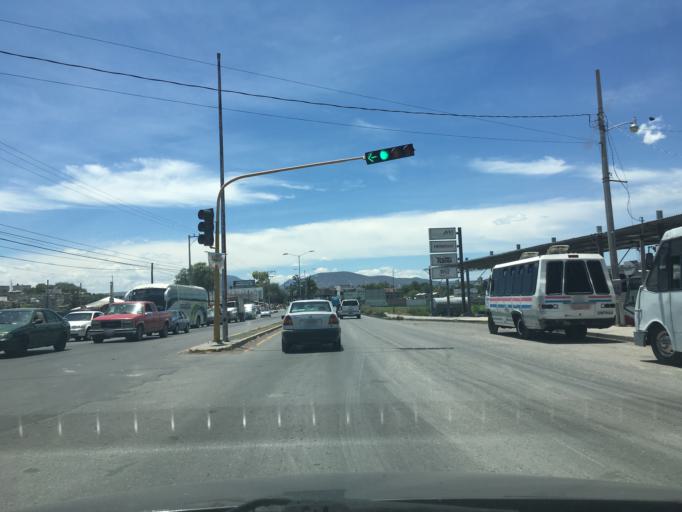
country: MX
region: Hidalgo
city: Ixmiquilpan
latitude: 20.4797
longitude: -99.2345
